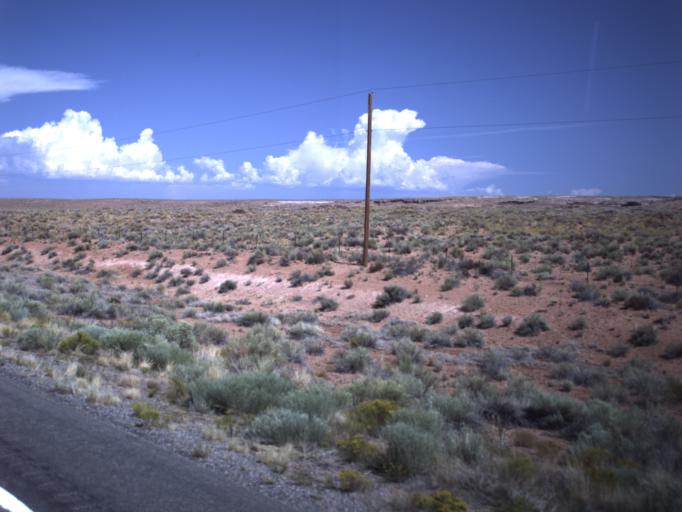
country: US
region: Utah
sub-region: San Juan County
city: Blanding
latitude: 37.1278
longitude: -109.5486
